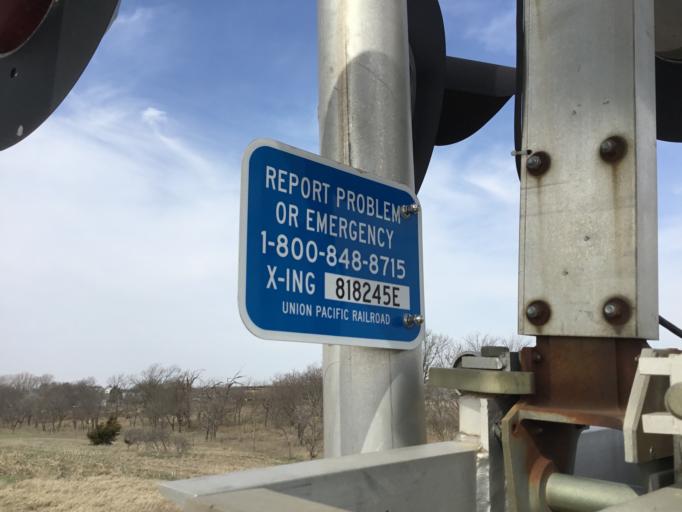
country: US
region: Kansas
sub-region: Ellsworth County
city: Ellsworth
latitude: 38.7268
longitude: -98.1273
